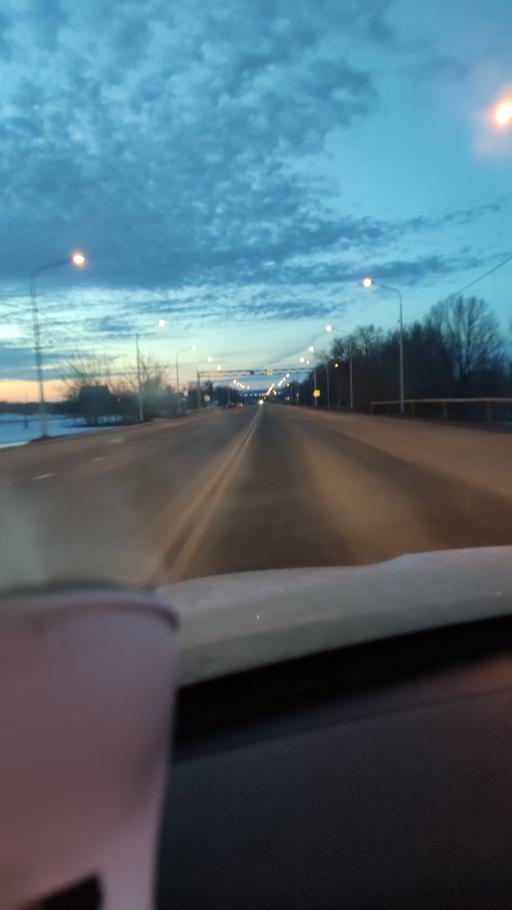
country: RU
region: Samara
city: Krasnoarmeyskoye
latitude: 52.8930
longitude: 49.9705
